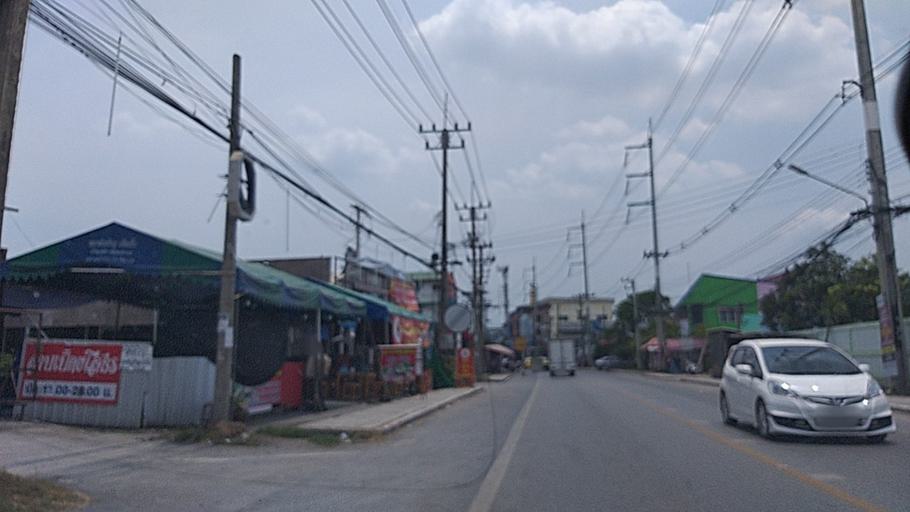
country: TH
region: Nakhon Pathom
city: Salaya
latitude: 13.7696
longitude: 100.2860
